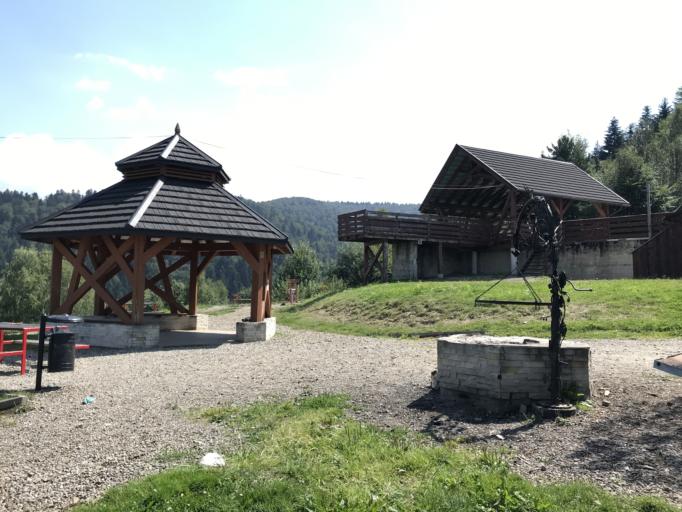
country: PL
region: Lesser Poland Voivodeship
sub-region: Powiat nowosadecki
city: Labowa
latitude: 49.5591
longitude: 20.8588
